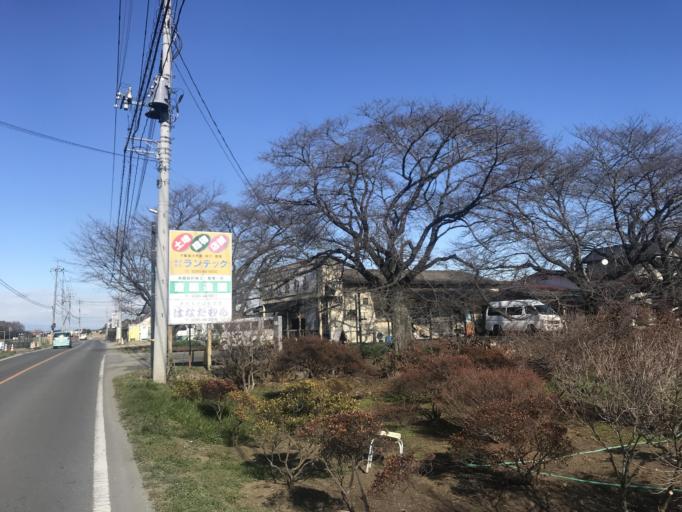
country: JP
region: Ibaraki
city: Yuki
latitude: 36.3611
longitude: 139.8767
